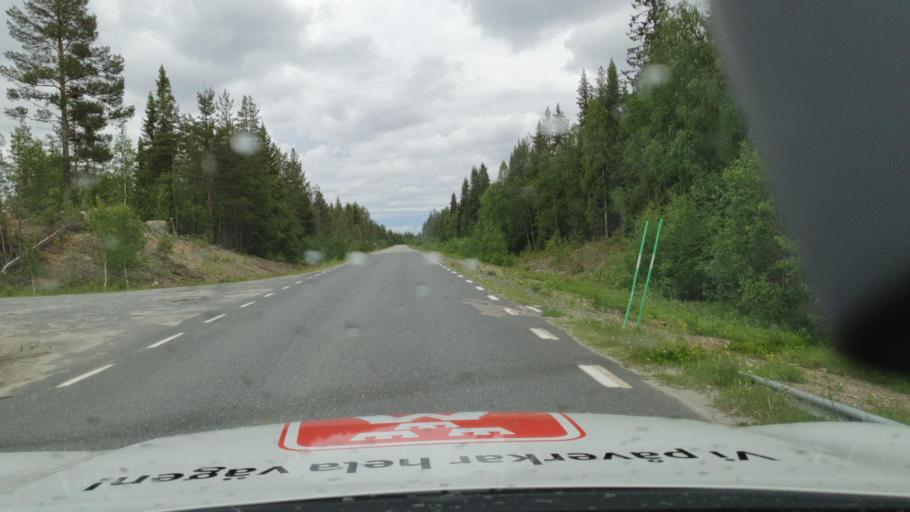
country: SE
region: Vaesterbotten
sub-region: Lycksele Kommun
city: Lycksele
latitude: 64.2439
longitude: 18.2205
